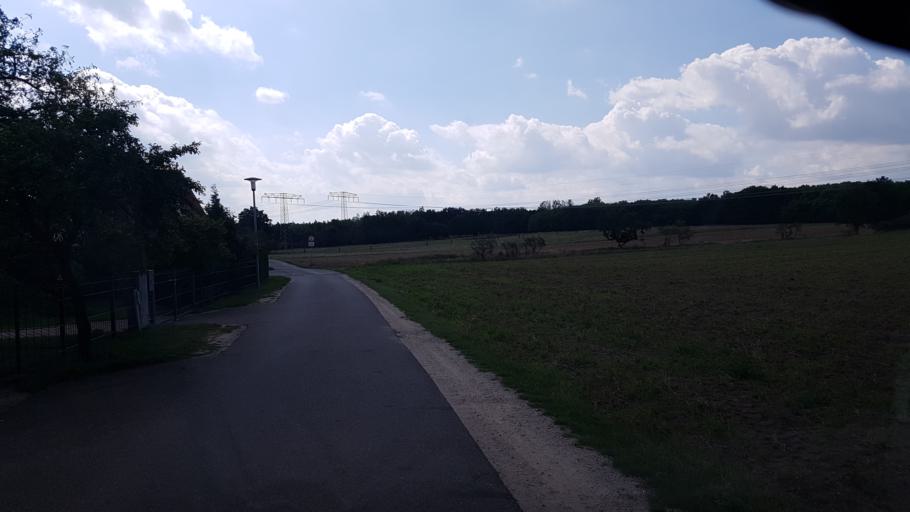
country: DE
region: Brandenburg
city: Lubbenau
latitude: 51.8667
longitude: 13.9161
